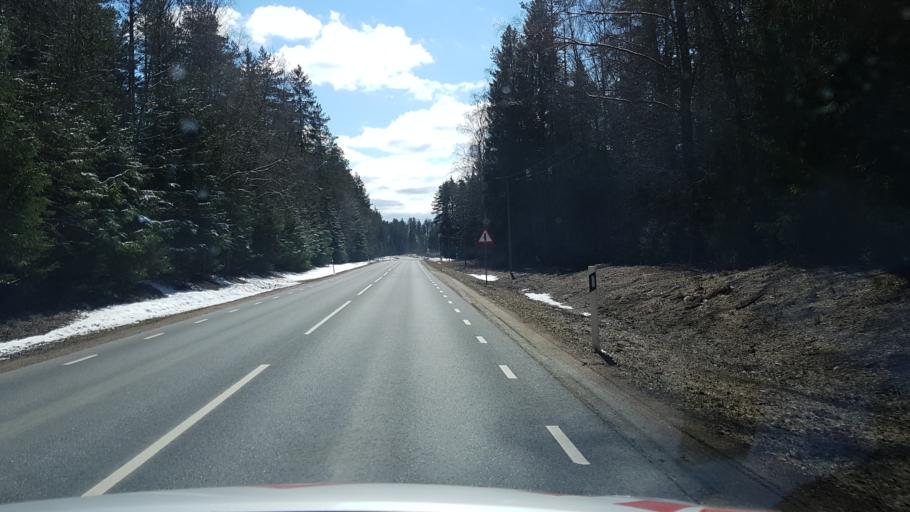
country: EE
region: Laeaene-Virumaa
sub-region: Kadrina vald
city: Kadrina
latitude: 59.3974
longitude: 26.0132
